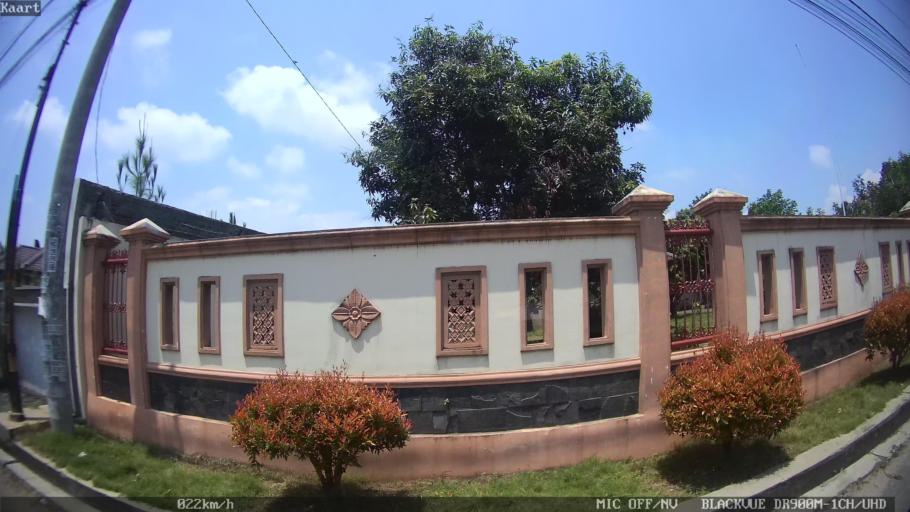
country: ID
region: Lampung
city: Kedaton
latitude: -5.3672
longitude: 105.2583
